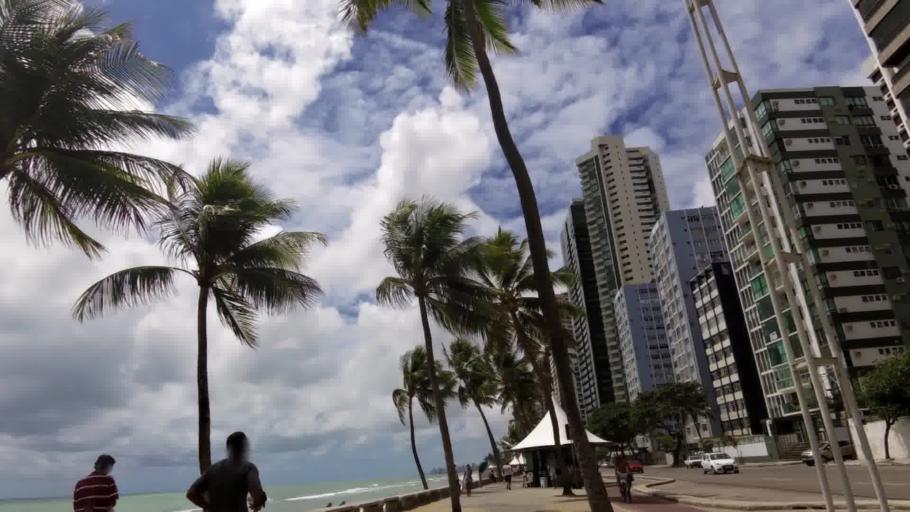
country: BR
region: Pernambuco
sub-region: Recife
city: Recife
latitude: -8.1338
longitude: -34.9006
